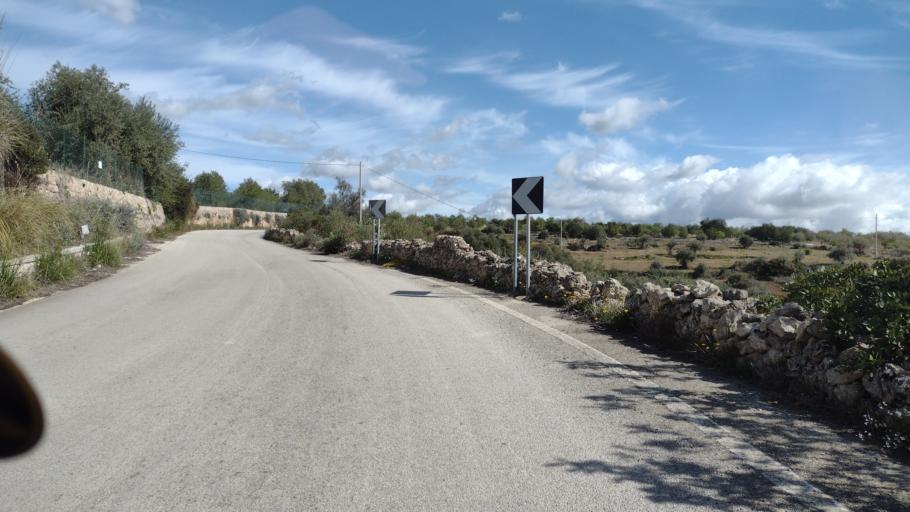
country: IT
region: Sicily
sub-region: Provincia di Siracusa
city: Noto
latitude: 36.8986
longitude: 15.0417
